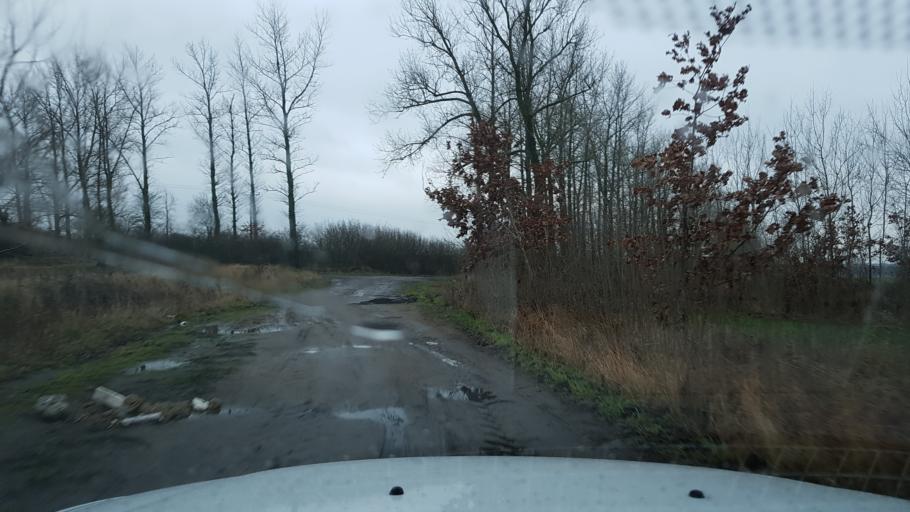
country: PL
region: West Pomeranian Voivodeship
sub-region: Powiat gryficki
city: Brojce
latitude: 53.9855
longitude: 15.3117
